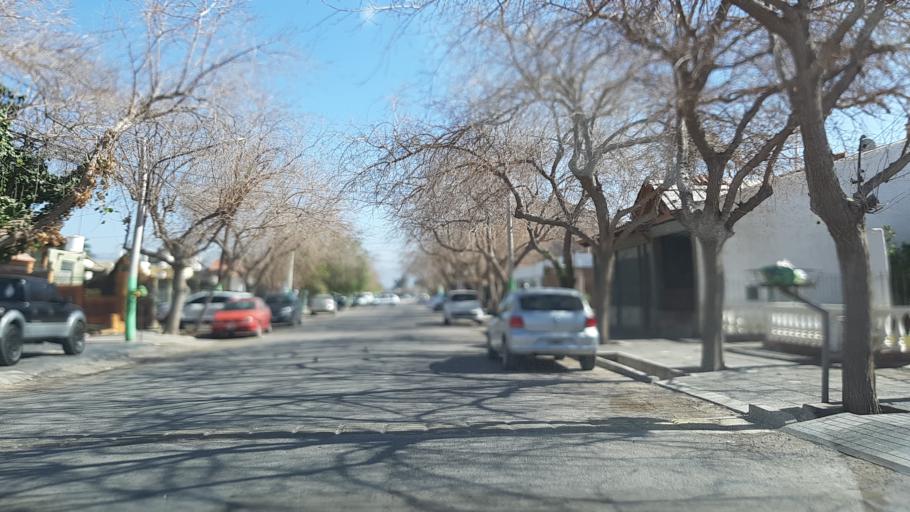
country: AR
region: San Juan
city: San Juan
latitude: -31.5364
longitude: -68.5813
